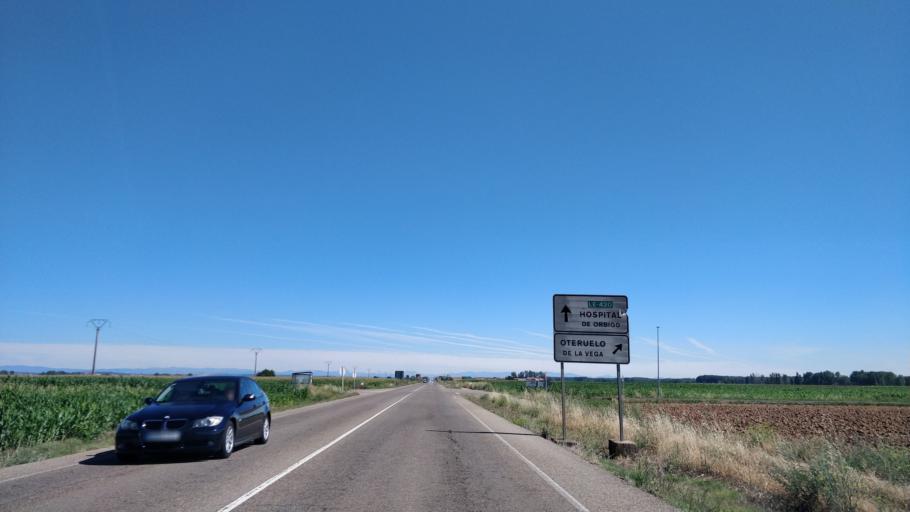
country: ES
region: Castille and Leon
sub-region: Provincia de Leon
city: Soto de la Vega
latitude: 42.3628
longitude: -5.8898
